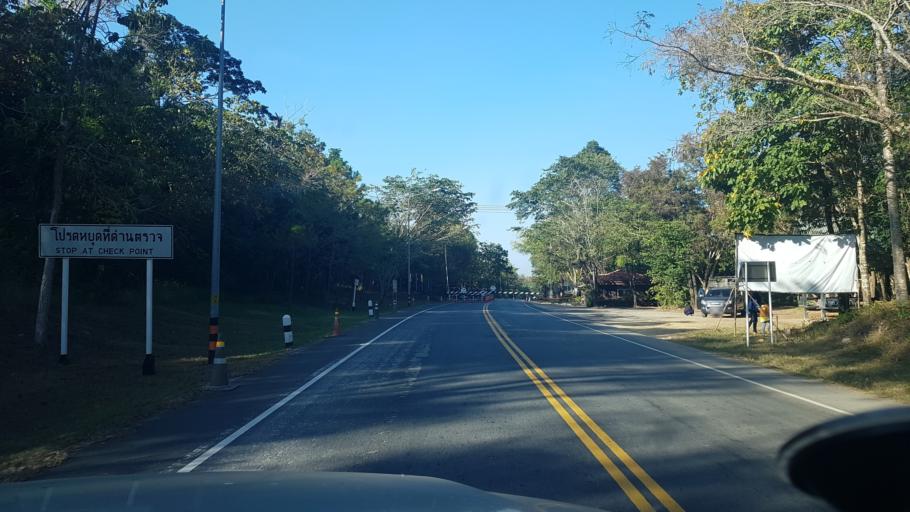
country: TH
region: Phetchabun
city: Lom Sak
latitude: 16.7374
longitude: 101.4403
